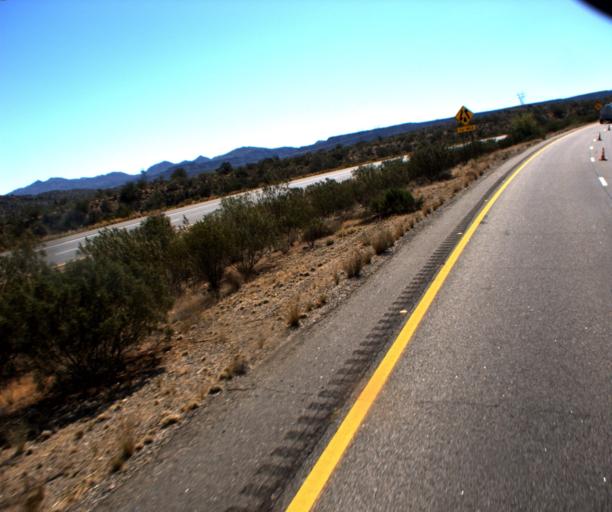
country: US
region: Arizona
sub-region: Yavapai County
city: Bagdad
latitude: 34.3674
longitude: -113.1796
